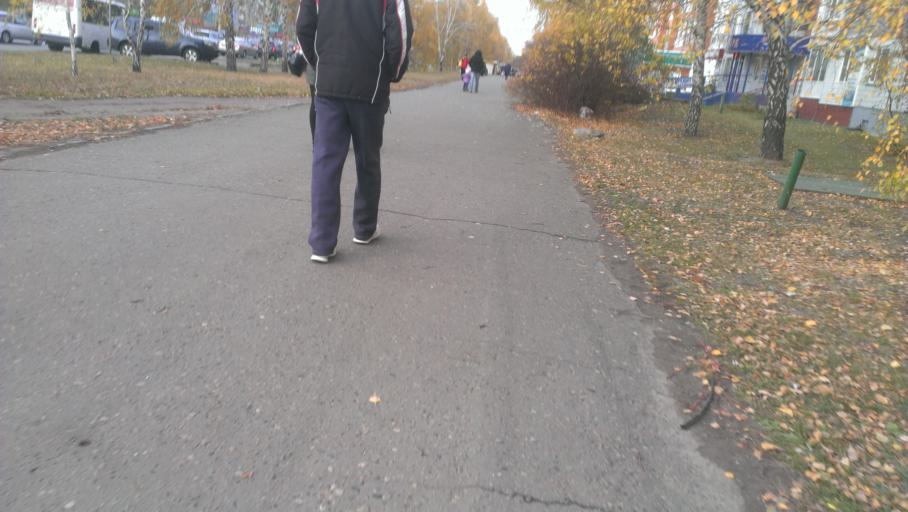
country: RU
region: Altai Krai
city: Novosilikatnyy
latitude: 53.3402
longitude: 83.6707
